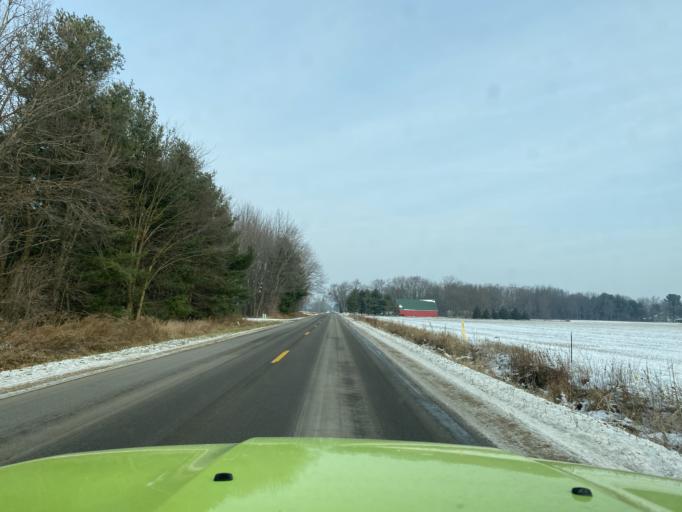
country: US
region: Michigan
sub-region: Ottawa County
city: Allendale
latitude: 42.9598
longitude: -85.9240
